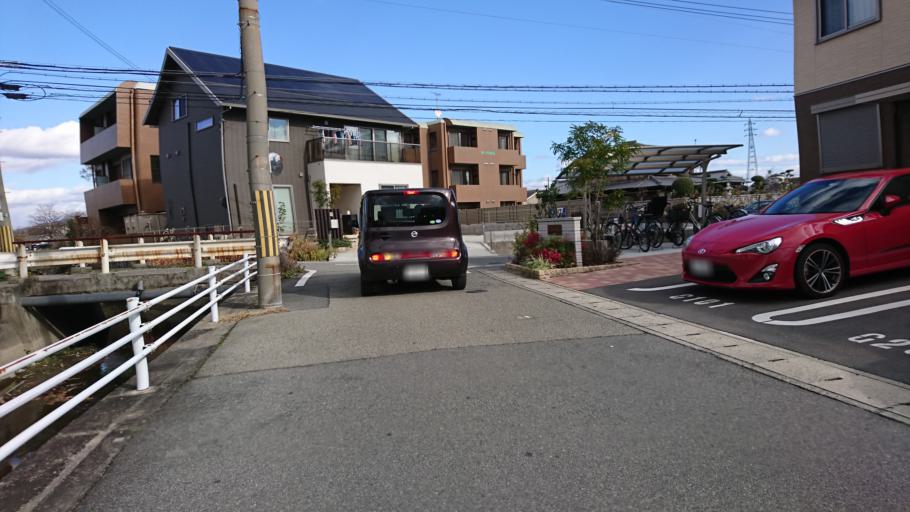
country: JP
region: Hyogo
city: Kakogawacho-honmachi
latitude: 34.7878
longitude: 134.8070
